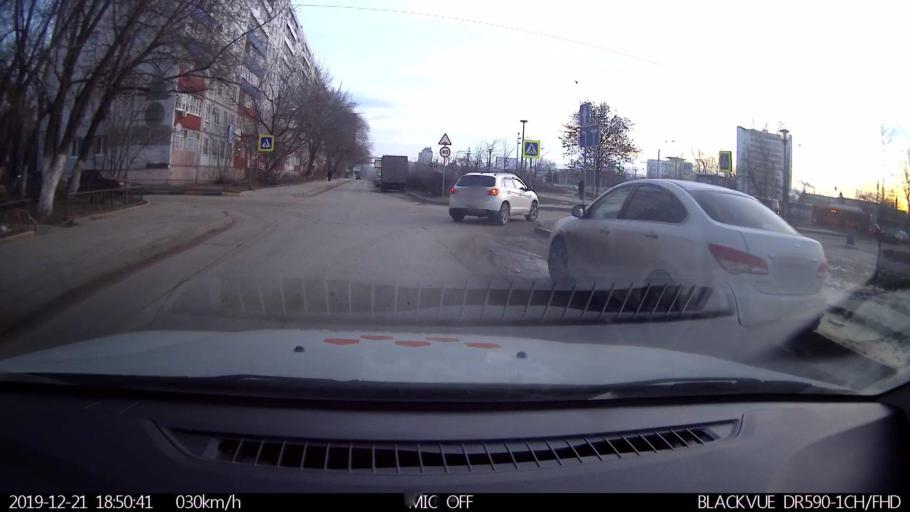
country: RU
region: Nizjnij Novgorod
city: Nizhniy Novgorod
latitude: 56.3219
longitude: 43.9389
